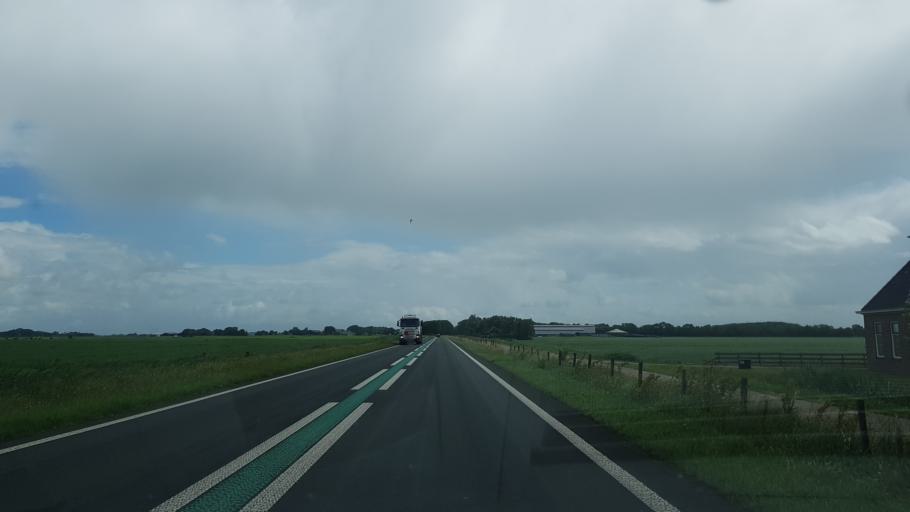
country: NL
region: Friesland
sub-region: Gemeente Dantumadiel
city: Rinsumageast
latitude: 53.2909
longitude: 5.9268
